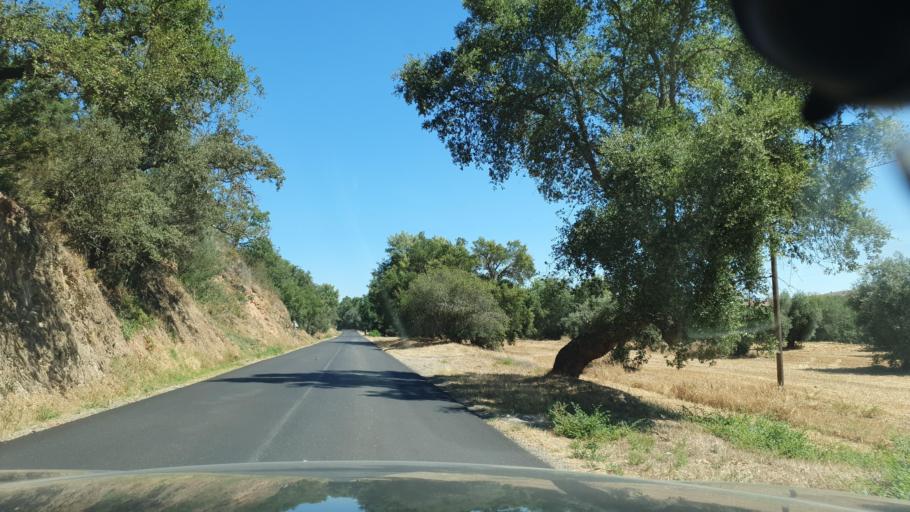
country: PT
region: Faro
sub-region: Monchique
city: Monchique
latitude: 37.4713
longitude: -8.4897
